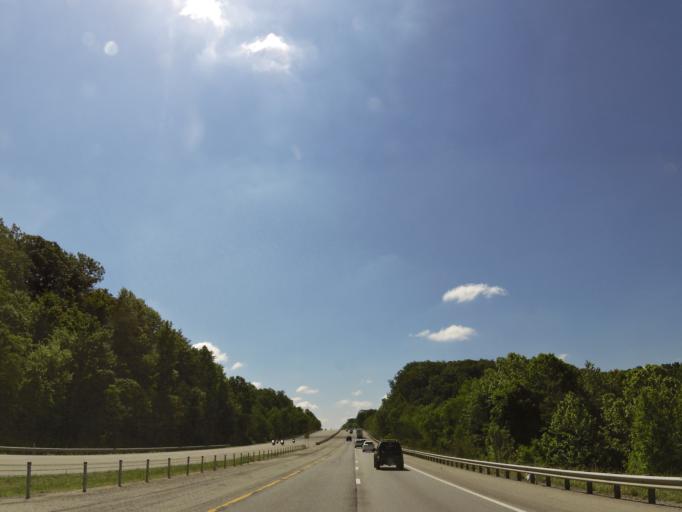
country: US
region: Kentucky
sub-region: Rockcastle County
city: Mount Vernon
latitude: 37.2987
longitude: -84.2772
